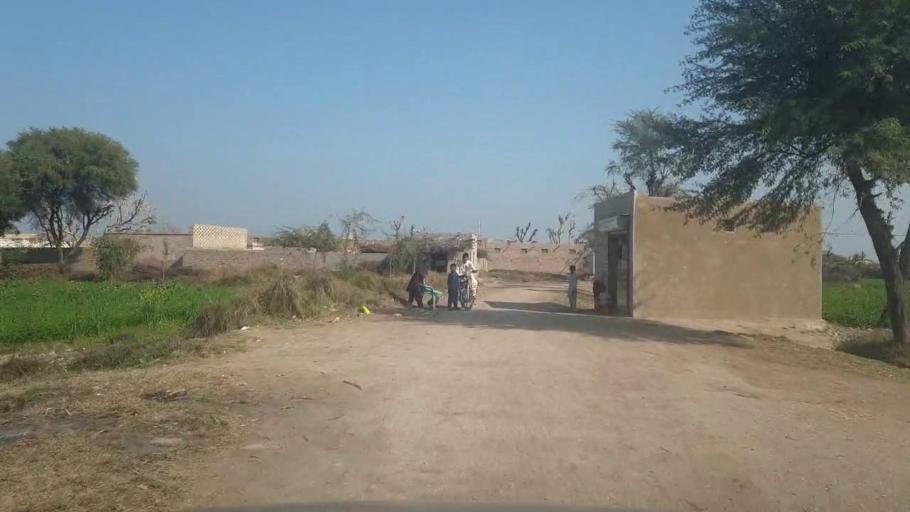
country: PK
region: Sindh
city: Sakrand
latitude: 26.0674
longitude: 68.4336
